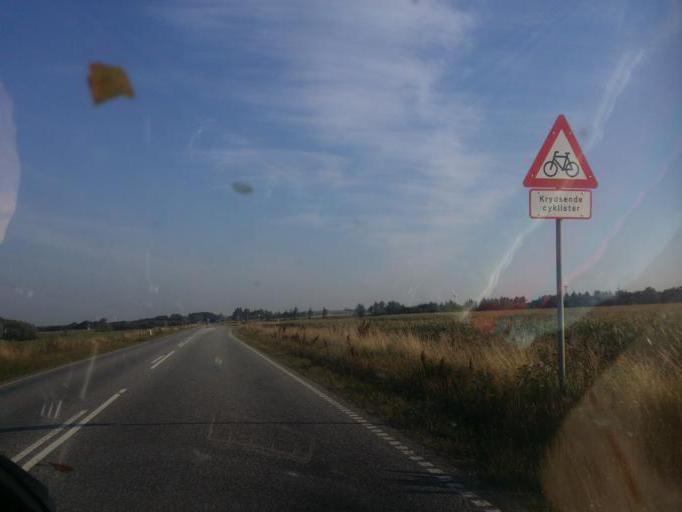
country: DK
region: South Denmark
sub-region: Tonder Kommune
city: Sherrebek
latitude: 55.1257
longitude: 8.8056
